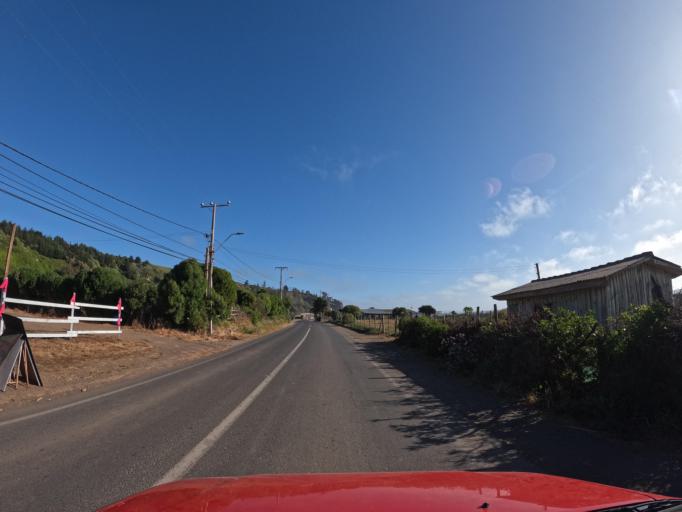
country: CL
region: Maule
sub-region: Provincia de Talca
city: Constitucion
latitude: -34.9001
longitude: -72.1795
